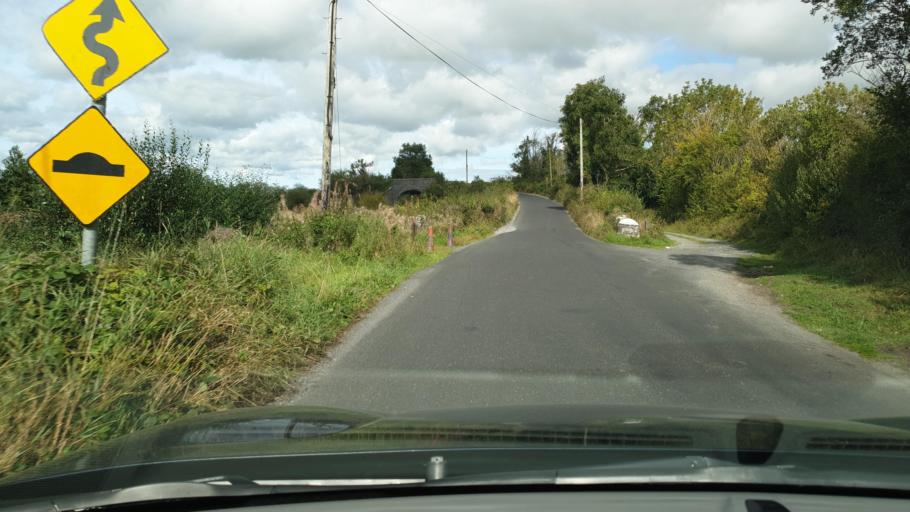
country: IE
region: Leinster
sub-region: Laois
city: Portlaoise
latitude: 53.0707
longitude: -7.2700
